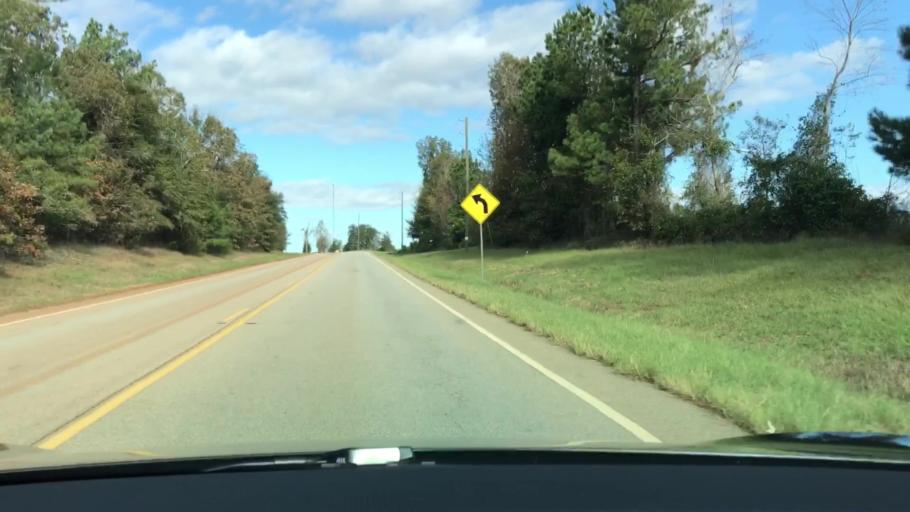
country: US
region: Georgia
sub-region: Jefferson County
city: Louisville
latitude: 33.0957
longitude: -82.4187
